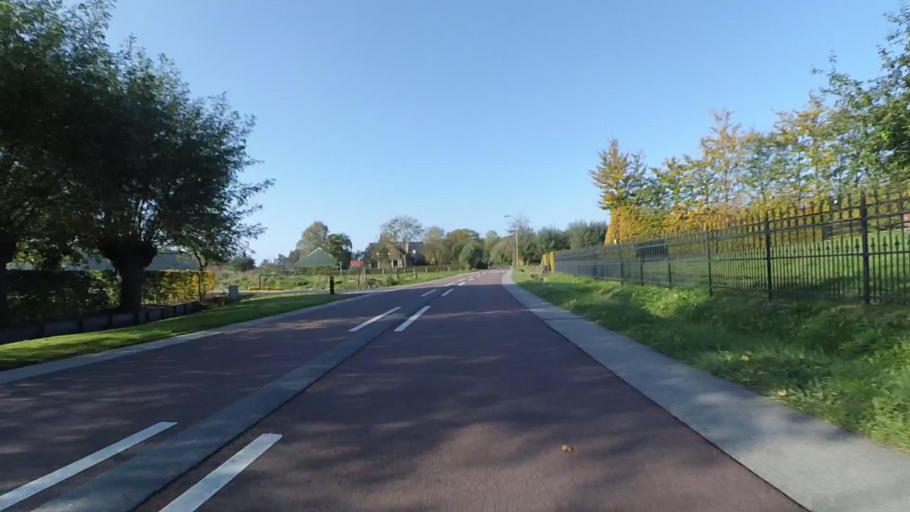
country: NL
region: Gelderland
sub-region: Gemeente Ermelo
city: Horst
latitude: 52.2639
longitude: 5.5499
